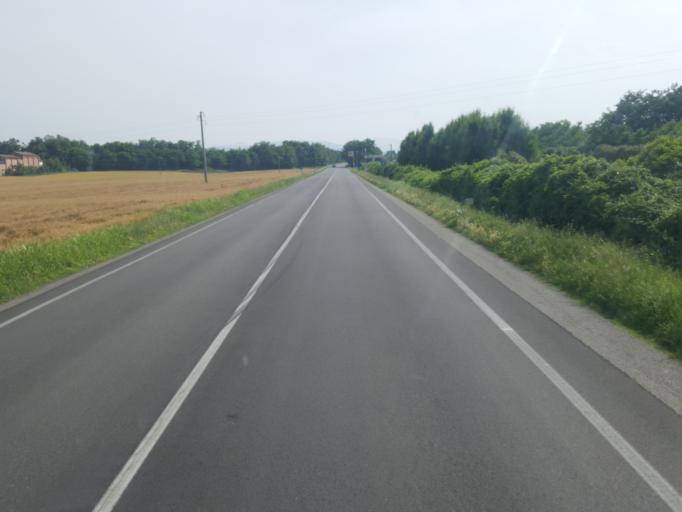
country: IT
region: Emilia-Romagna
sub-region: Provincia di Piacenza
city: Niviano
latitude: 44.9608
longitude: 9.6497
